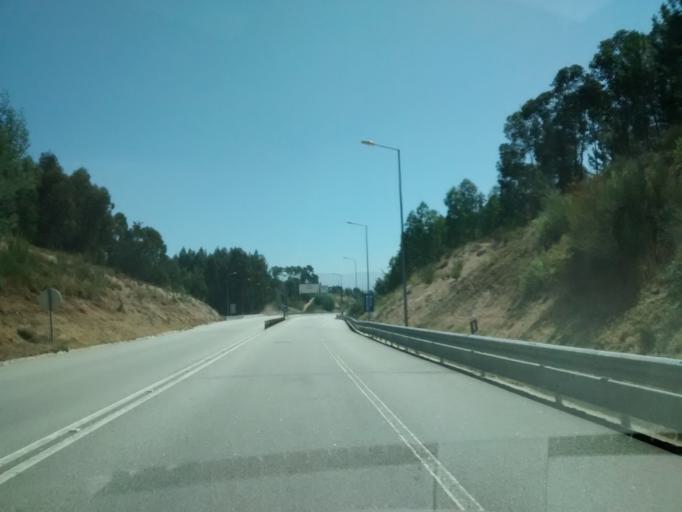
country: PT
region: Coimbra
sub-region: Tabua
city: Tabua
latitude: 40.3685
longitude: -8.0107
